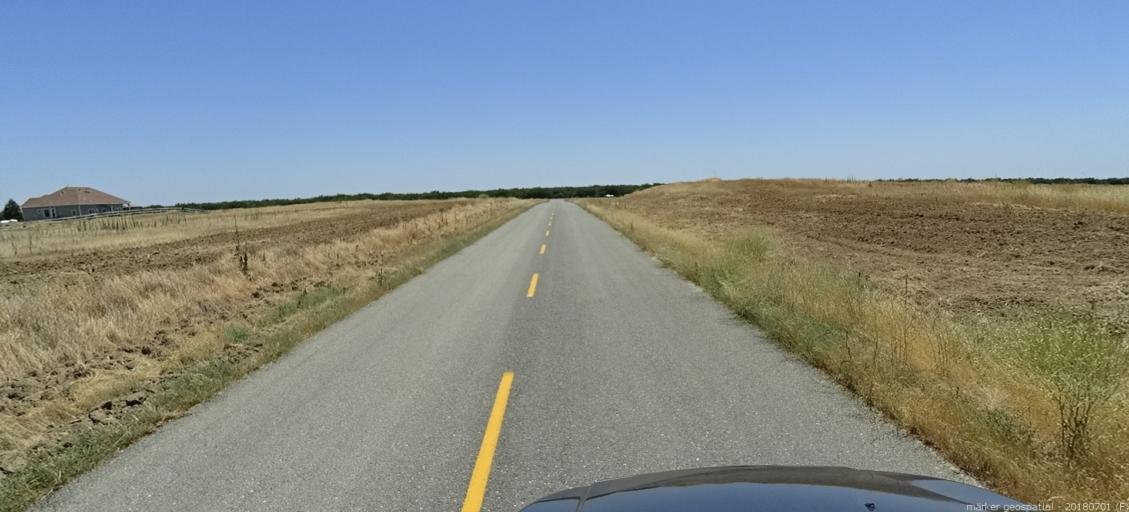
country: US
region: California
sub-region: Madera County
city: Madera Acres
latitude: 37.0566
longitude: -120.0181
